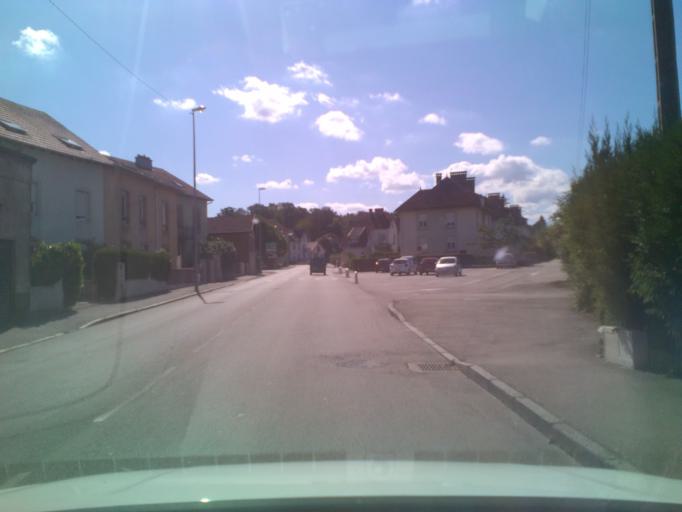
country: FR
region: Lorraine
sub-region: Departement des Vosges
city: Saint-Die-des-Vosges
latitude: 48.2790
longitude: 6.9523
